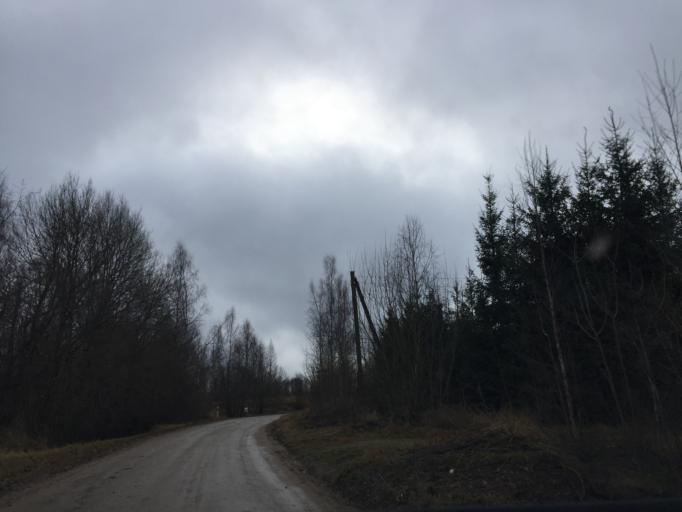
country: LV
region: Broceni
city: Broceni
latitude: 56.6596
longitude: 22.5550
